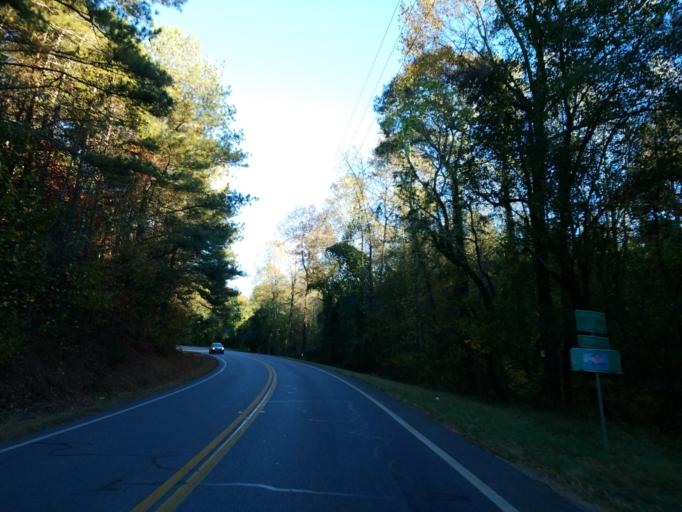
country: US
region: Georgia
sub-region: Dawson County
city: Dawsonville
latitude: 34.4190
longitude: -84.1426
